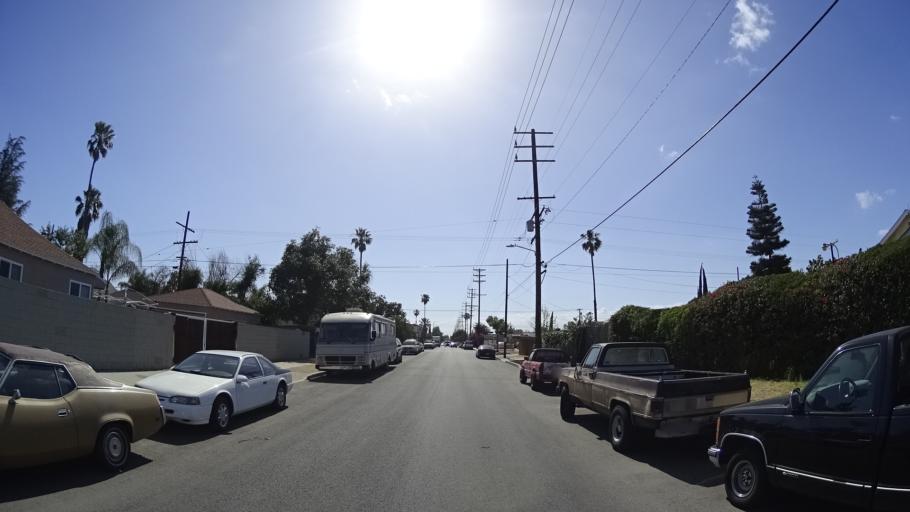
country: US
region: California
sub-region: Los Angeles County
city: North Hollywood
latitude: 34.1758
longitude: -118.3683
